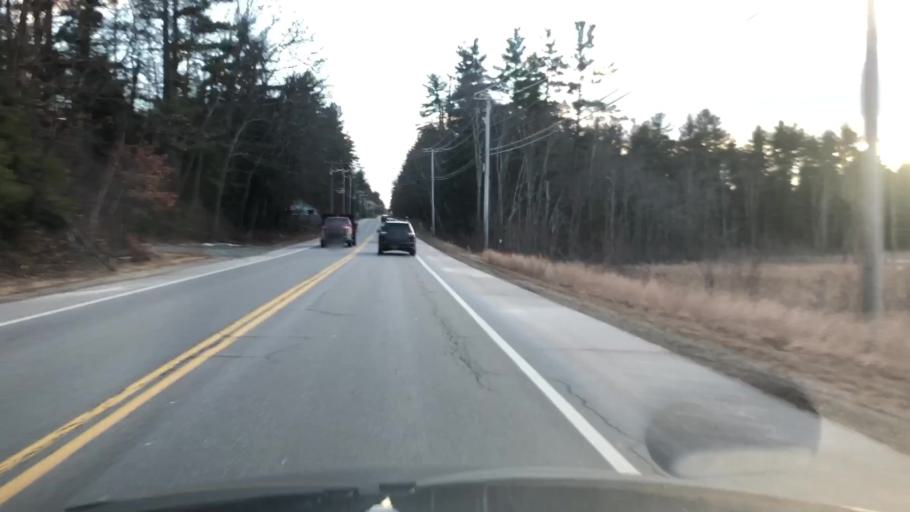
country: US
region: New Hampshire
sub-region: Hillsborough County
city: Milford
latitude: 42.8015
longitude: -71.6531
